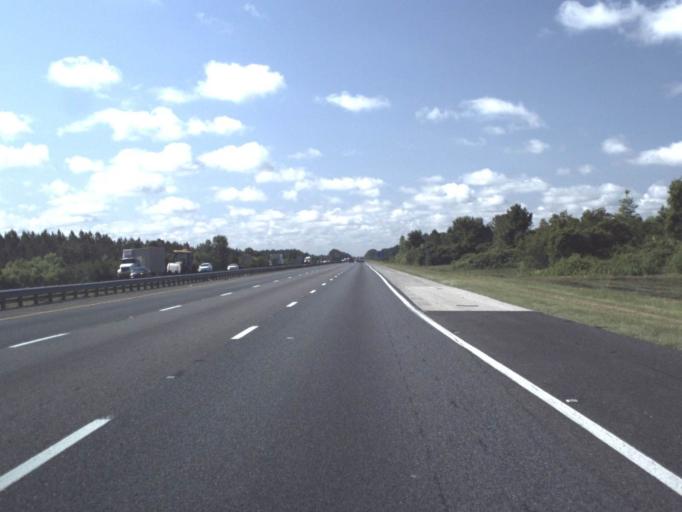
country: US
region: Florida
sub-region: Saint Johns County
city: Saint Augustine Shores
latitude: 29.7422
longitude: -81.3444
